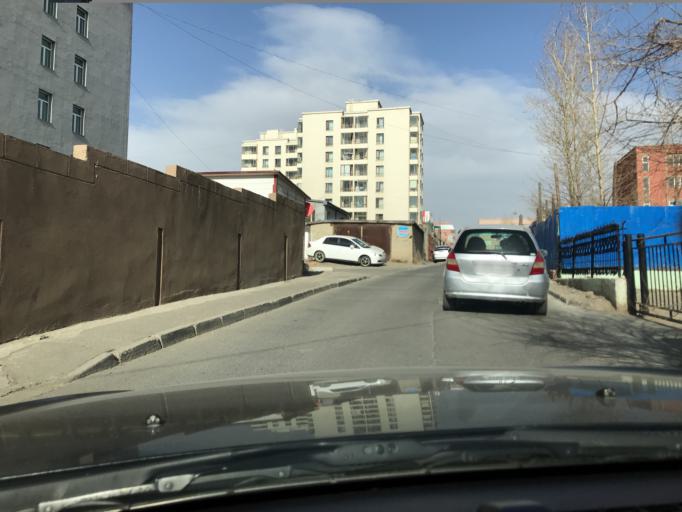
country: MN
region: Ulaanbaatar
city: Ulaanbaatar
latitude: 47.9203
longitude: 106.9400
